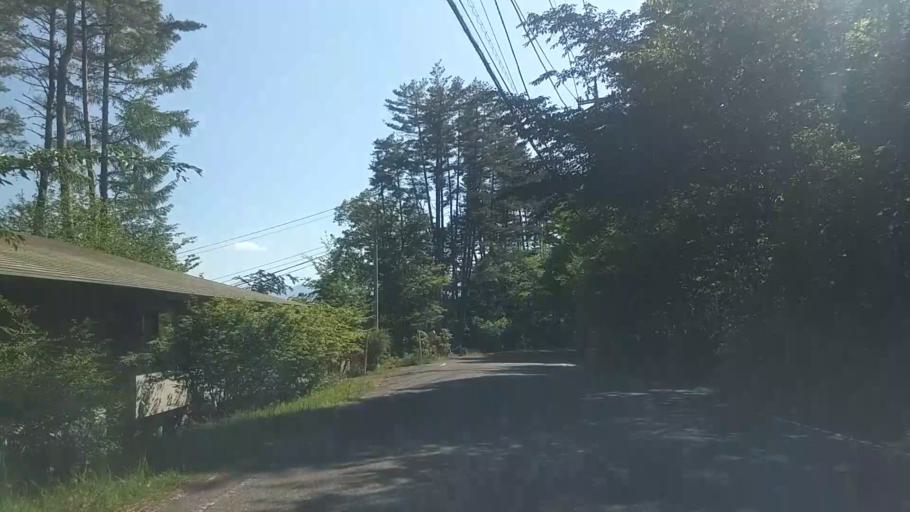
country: JP
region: Yamanashi
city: Nirasaki
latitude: 35.8918
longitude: 138.3982
